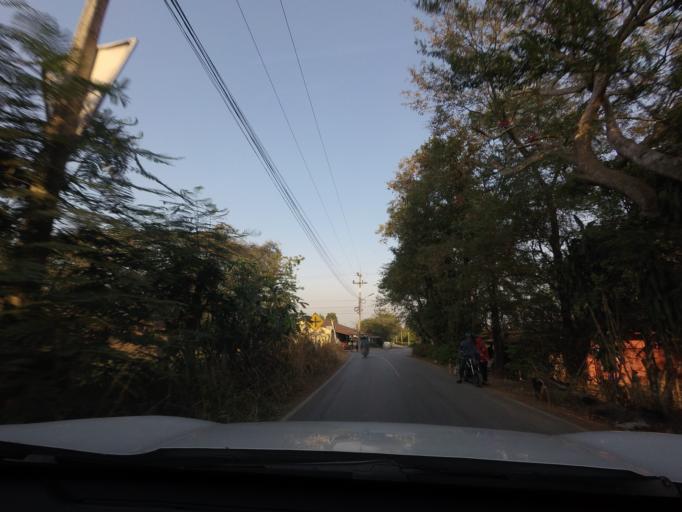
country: TH
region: Nakhon Ratchasima
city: Pak Chong
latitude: 14.6516
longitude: 101.3875
